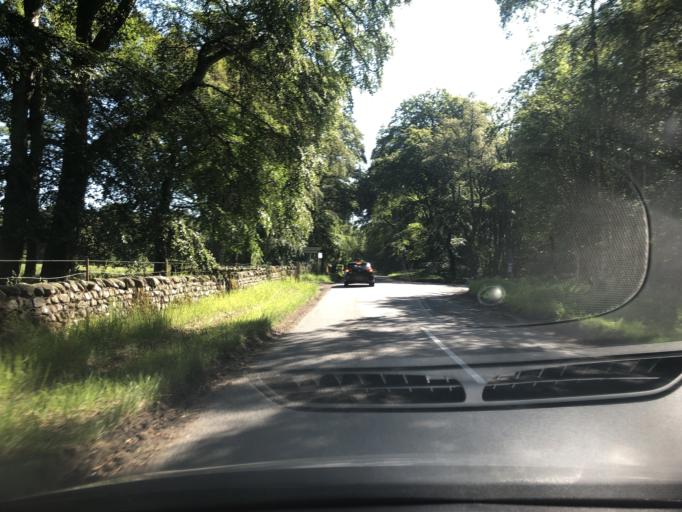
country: GB
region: Scotland
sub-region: Angus
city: Brechin
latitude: 56.8296
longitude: -2.6485
